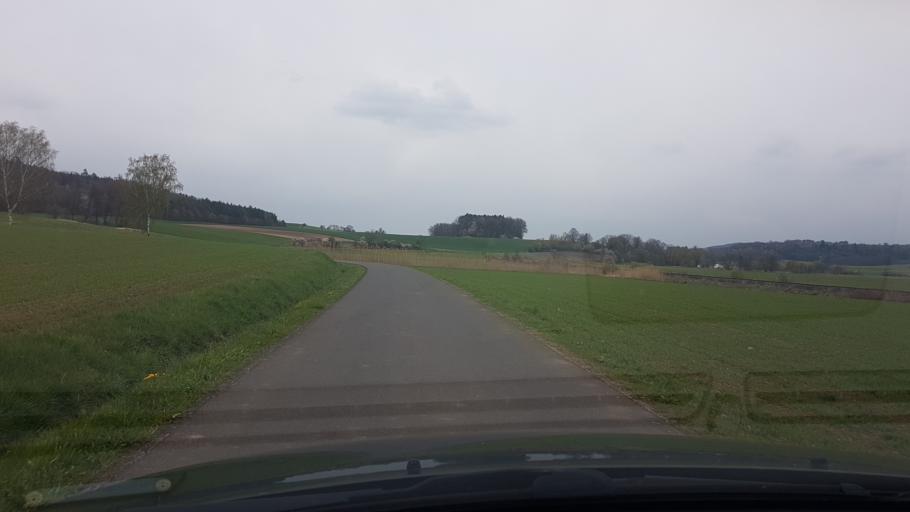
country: DE
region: Bavaria
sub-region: Regierungsbezirk Unterfranken
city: Rentweinsdorf
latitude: 50.0575
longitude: 10.8173
